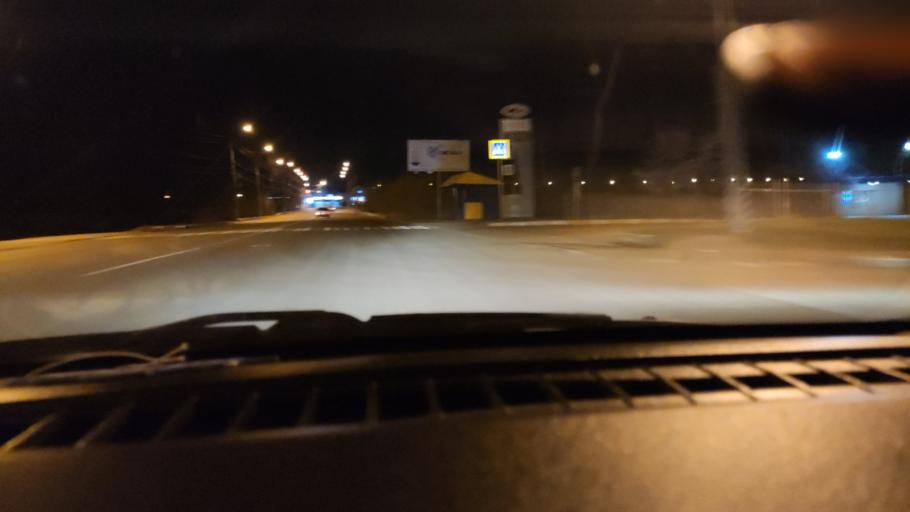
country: RU
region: Saratov
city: Privolzhskiy
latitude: 51.4228
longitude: 46.0470
